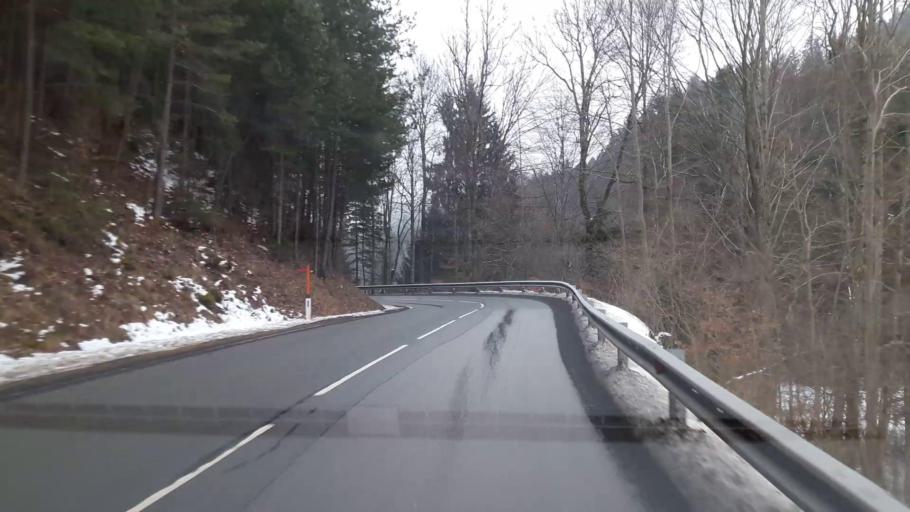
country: AT
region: Lower Austria
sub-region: Politischer Bezirk Neunkirchen
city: Feistritz am Wechsel
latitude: 47.5603
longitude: 16.0568
